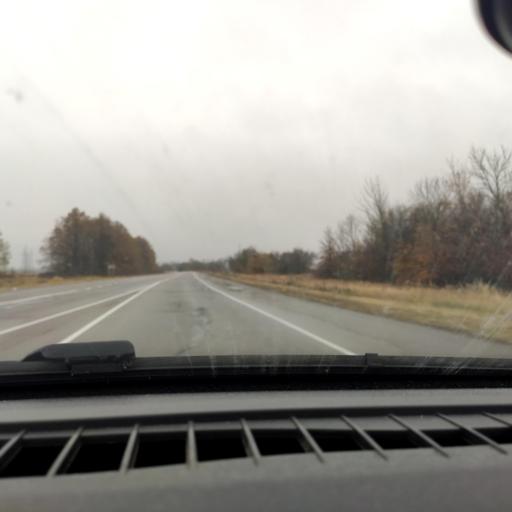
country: RU
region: Voronezj
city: Kolodeznyy
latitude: 51.3212
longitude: 39.0276
